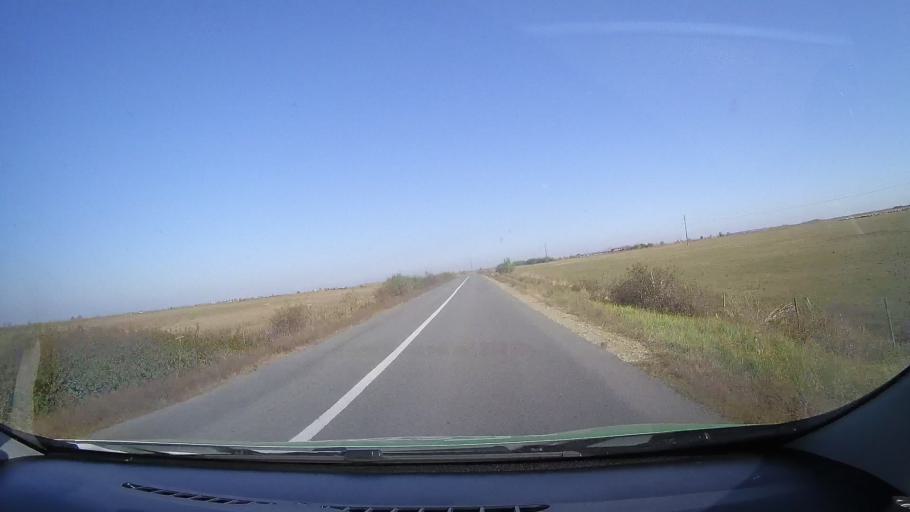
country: RO
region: Satu Mare
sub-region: Comuna Cauas
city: Cauas
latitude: 47.5397
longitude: 22.5639
